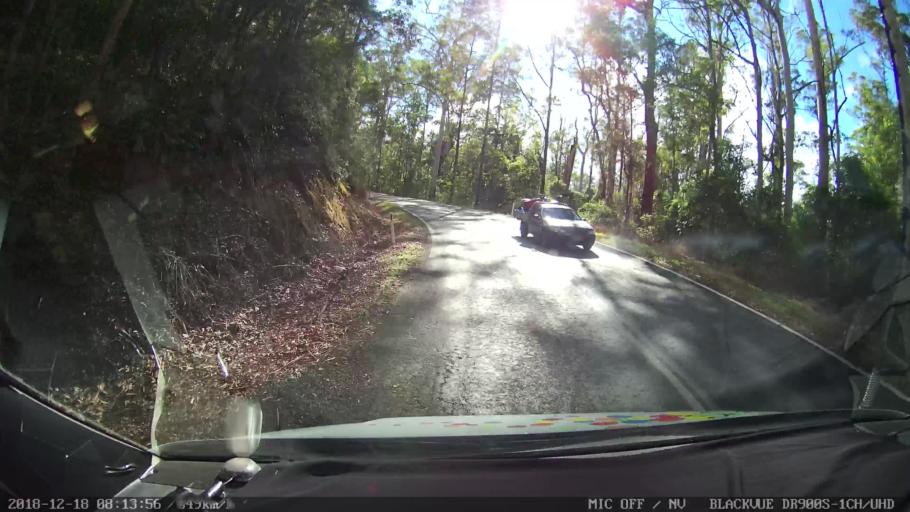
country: AU
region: New South Wales
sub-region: Kyogle
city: Kyogle
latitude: -28.3375
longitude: 152.6791
